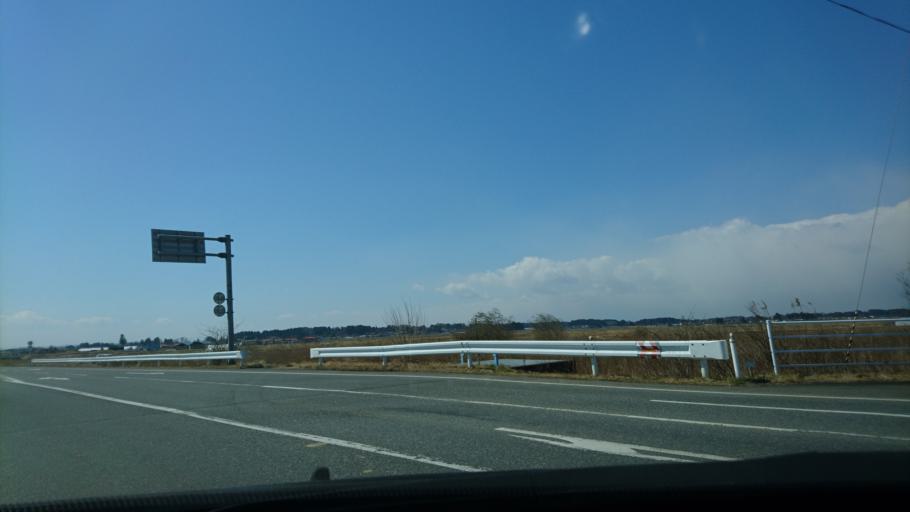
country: JP
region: Iwate
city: Ichinoseki
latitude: 38.7630
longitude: 141.1308
